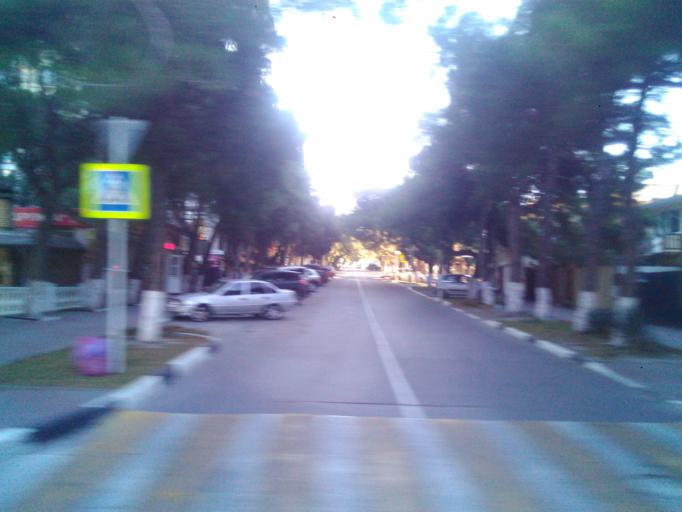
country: RU
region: Krasnodarskiy
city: Gelendzhik
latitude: 44.5539
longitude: 38.0735
